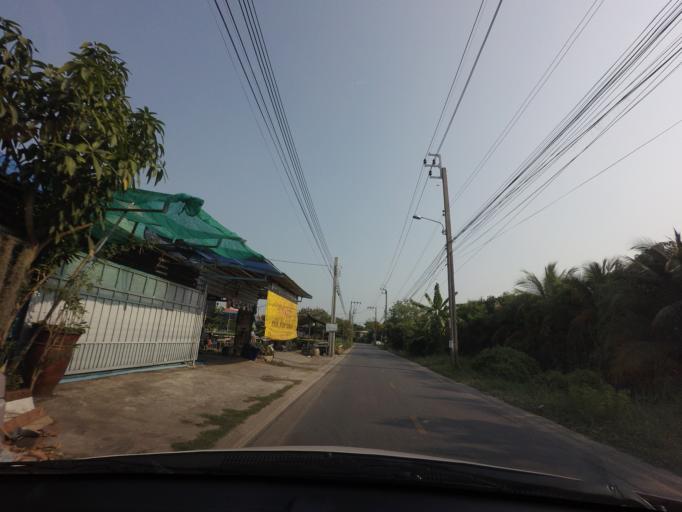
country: TH
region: Nonthaburi
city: Bang Yai
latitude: 13.8047
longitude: 100.3734
